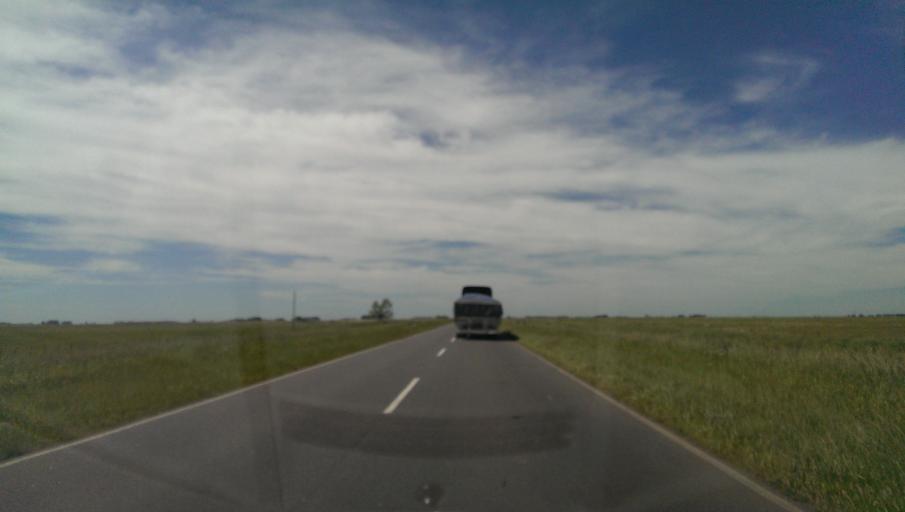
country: AR
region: Buenos Aires
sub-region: Partido de Laprida
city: Laprida
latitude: -37.2428
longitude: -60.7844
